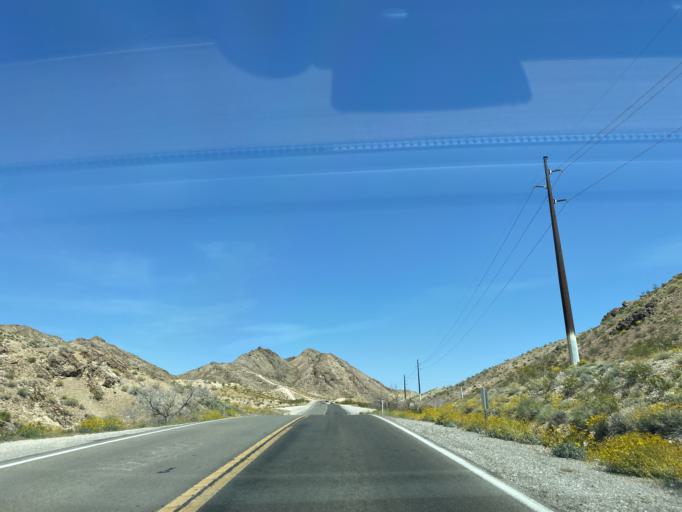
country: US
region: Nevada
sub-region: Clark County
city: Nellis Air Force Base
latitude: 36.2006
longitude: -114.9951
